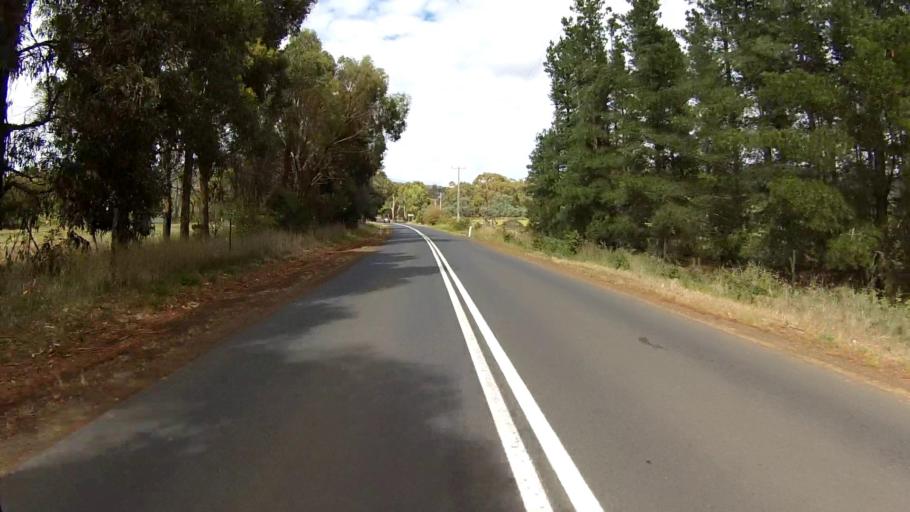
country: AU
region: Tasmania
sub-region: Clarence
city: Cambridge
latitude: -42.7632
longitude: 147.3950
